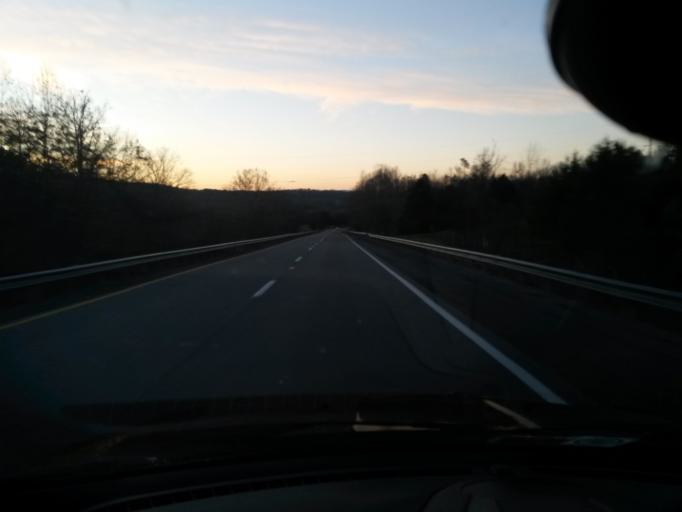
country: US
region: Virginia
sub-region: Botetourt County
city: Fincastle
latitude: 37.5838
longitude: -79.8330
